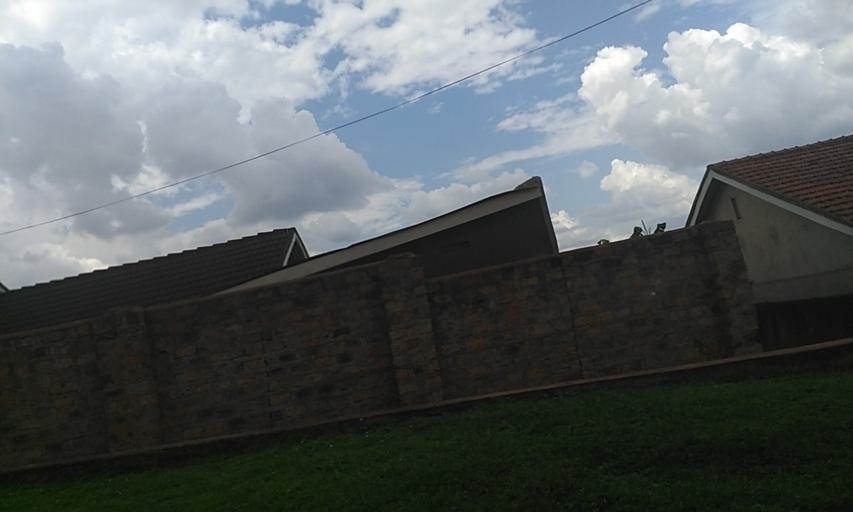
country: UG
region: Central Region
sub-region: Wakiso District
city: Kireka
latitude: 0.3556
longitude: 32.6109
